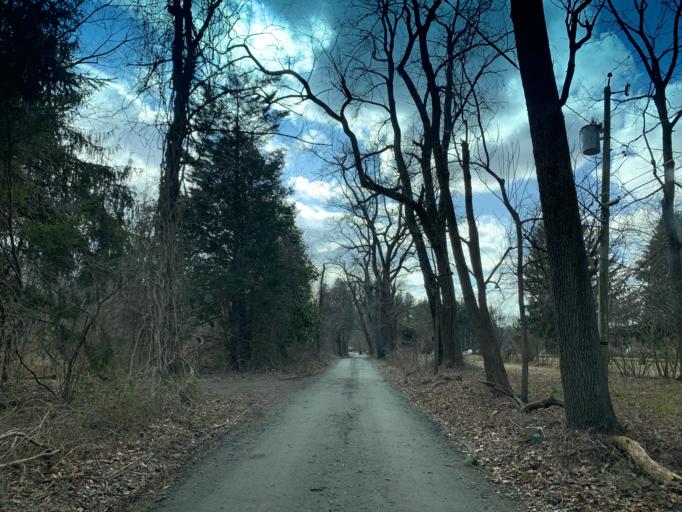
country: US
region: Maryland
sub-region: Harford County
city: Riverside
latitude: 39.5059
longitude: -76.2500
